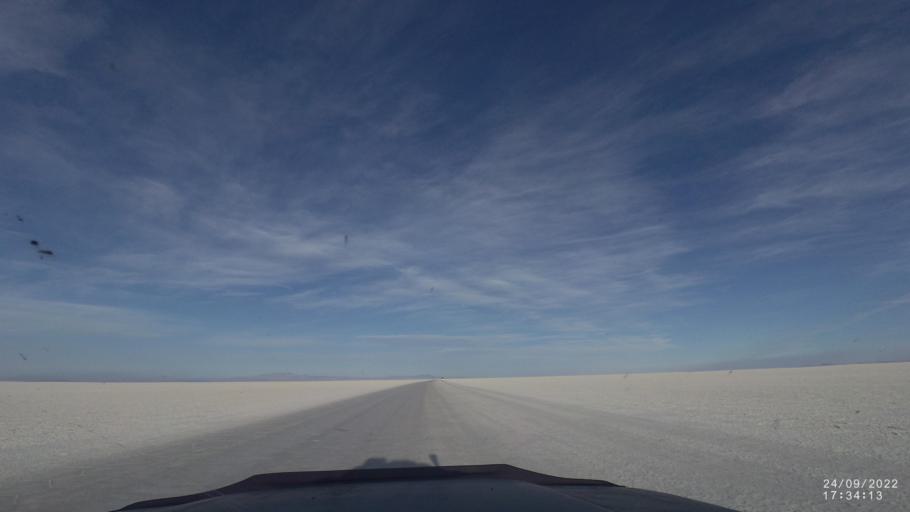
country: BO
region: Potosi
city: Colchani
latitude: -20.3204
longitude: -67.2873
